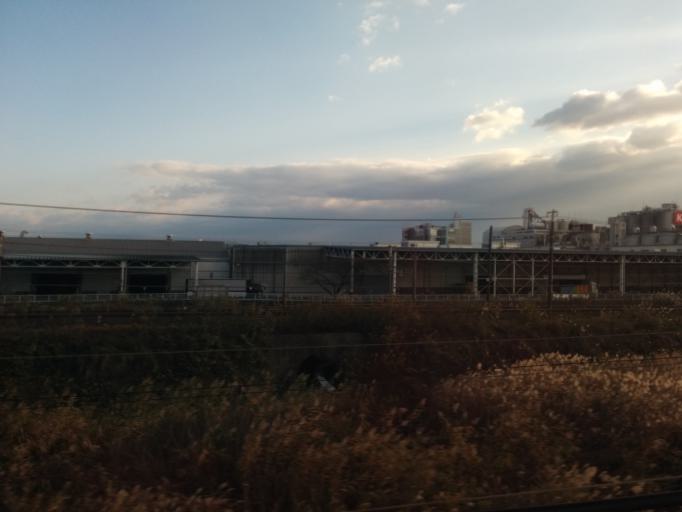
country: JP
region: Aichi
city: Nagoya-shi
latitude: 35.2090
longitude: 136.8483
